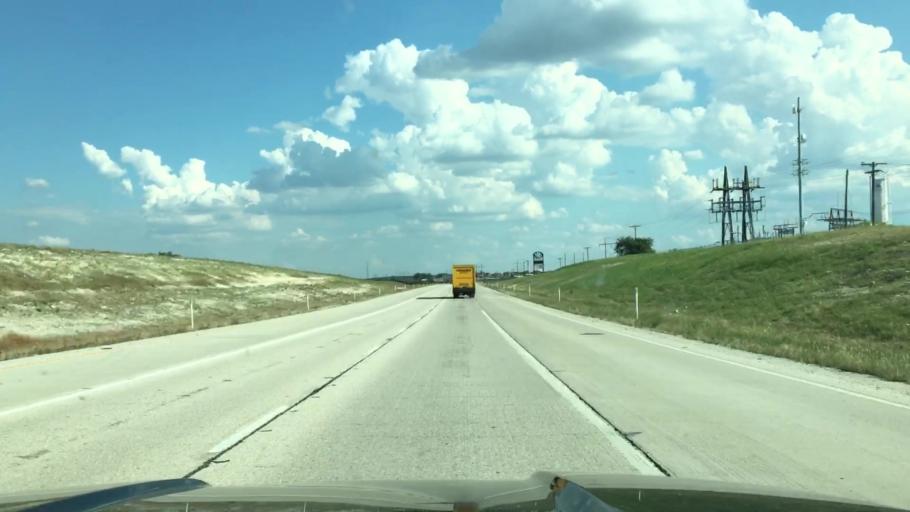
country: US
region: Texas
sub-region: Wise County
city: Decatur
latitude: 33.1794
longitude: -97.5472
